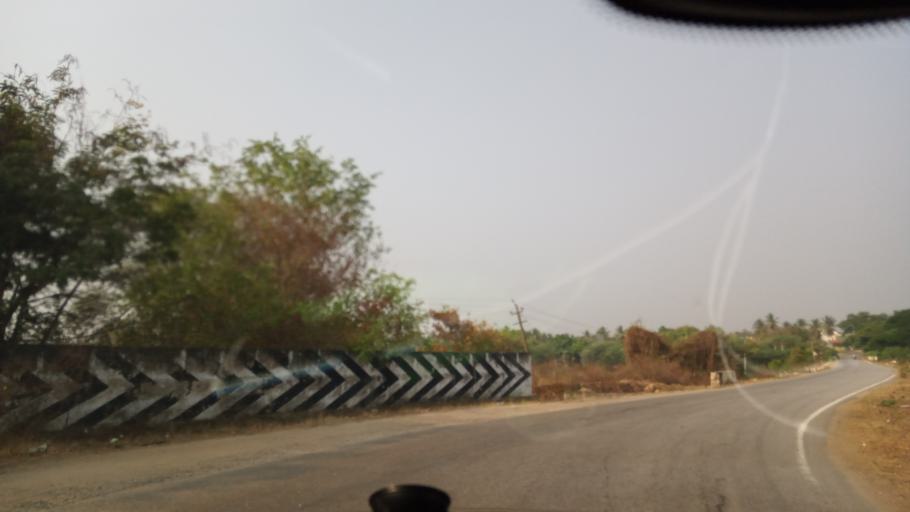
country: IN
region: Karnataka
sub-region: Mandya
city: Belluru
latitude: 12.9621
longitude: 76.7631
